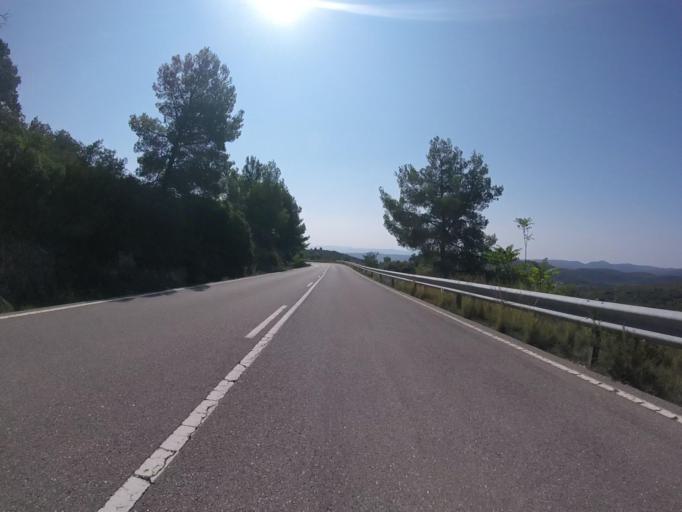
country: ES
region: Valencia
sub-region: Provincia de Castello
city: Benafigos
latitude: 40.2642
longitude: -0.2221
